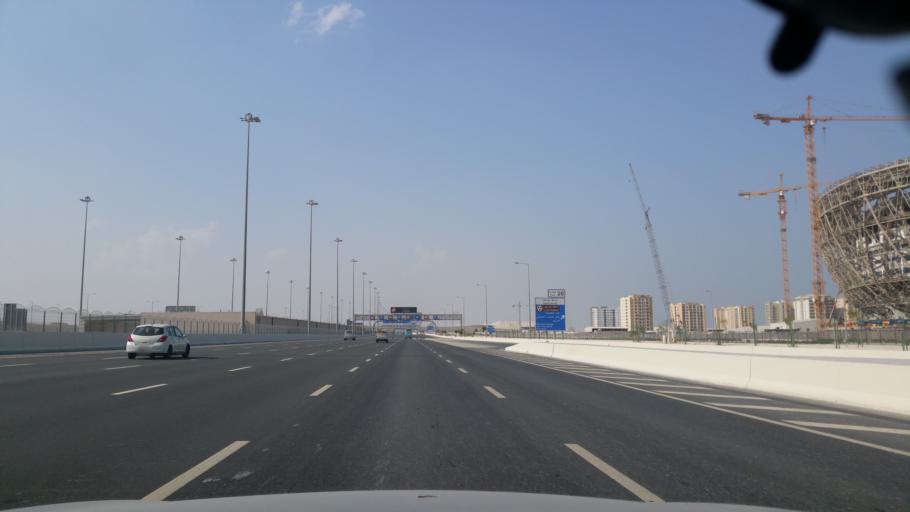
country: QA
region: Baladiyat Umm Salal
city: Umm Salal Muhammad
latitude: 25.4173
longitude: 51.4877
